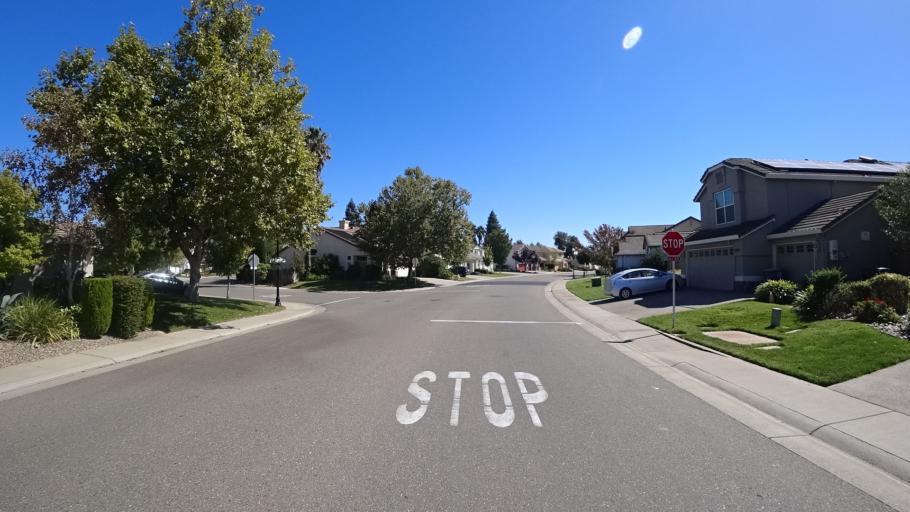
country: US
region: California
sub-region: Sacramento County
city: Laguna
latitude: 38.4155
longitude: -121.4626
